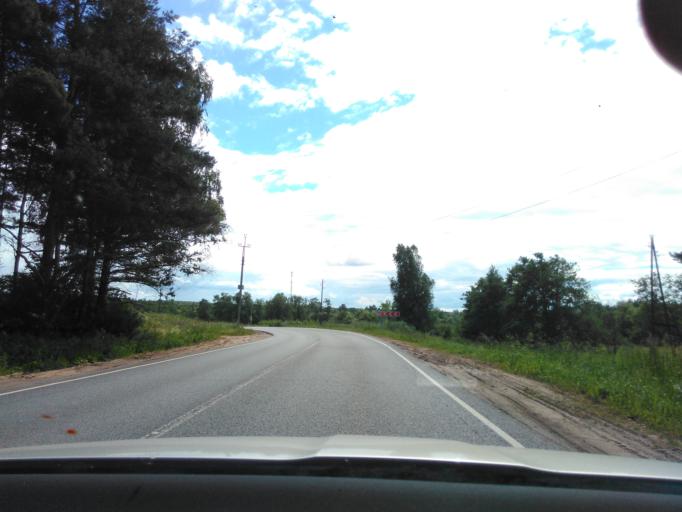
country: RU
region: Moskovskaya
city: Shevlyakovo
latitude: 56.4115
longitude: 36.8744
